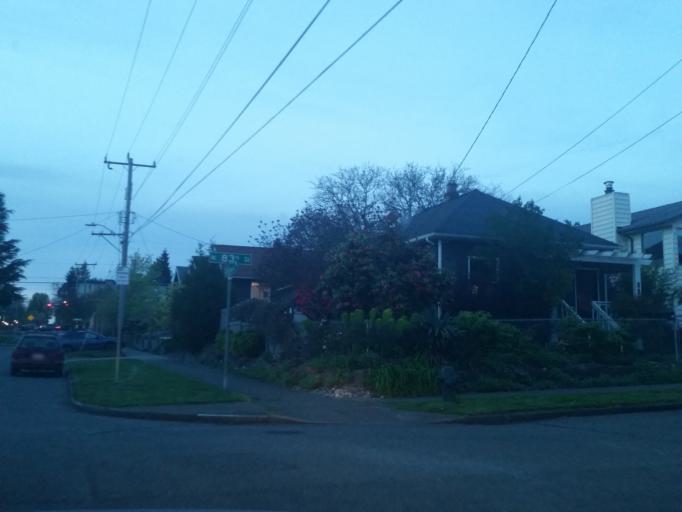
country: US
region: Washington
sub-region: King County
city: Shoreline
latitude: 47.6890
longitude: -122.3526
